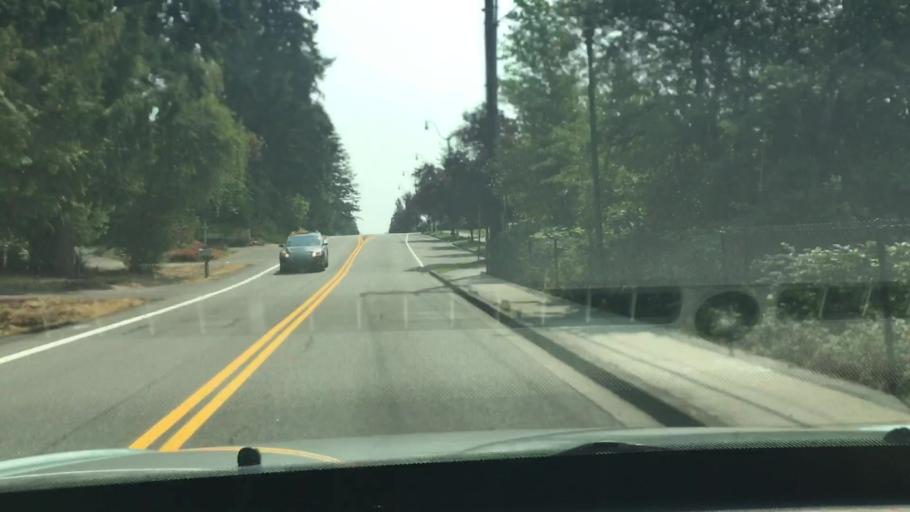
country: US
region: Washington
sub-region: King County
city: City of Sammamish
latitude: 47.5947
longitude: -122.0570
